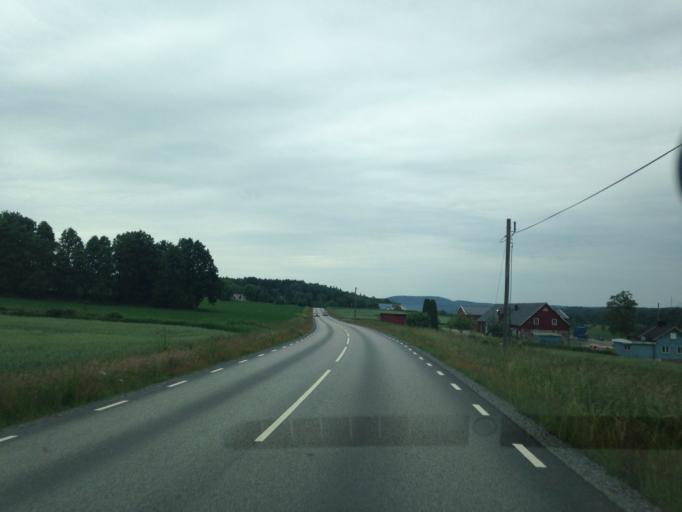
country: SE
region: Vaestra Goetaland
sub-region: Marks Kommun
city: Horred
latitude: 57.4904
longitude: 12.5244
